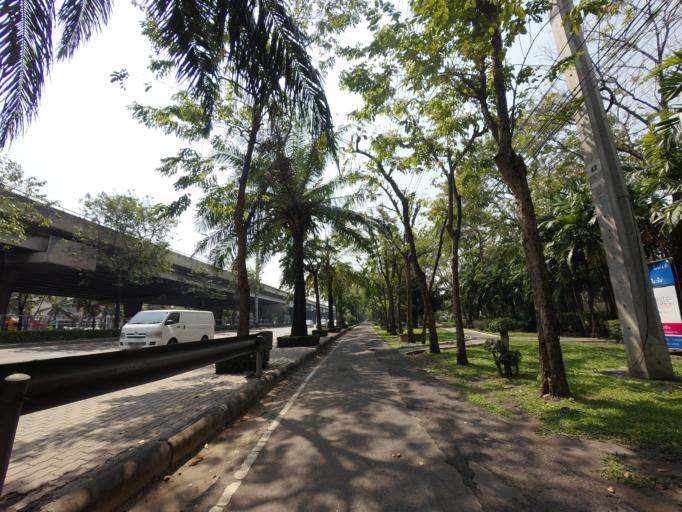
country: TH
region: Bangkok
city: Wang Thonglang
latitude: 13.7817
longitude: 100.6074
